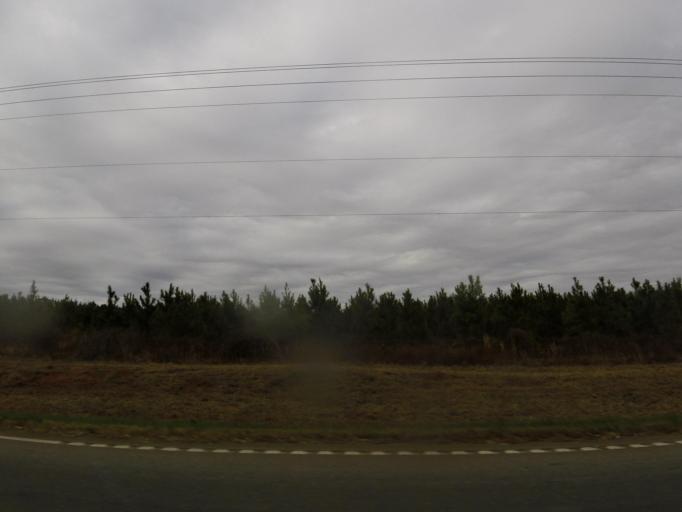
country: US
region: Georgia
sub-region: Randolph County
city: Cuthbert
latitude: 31.7751
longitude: -84.7469
